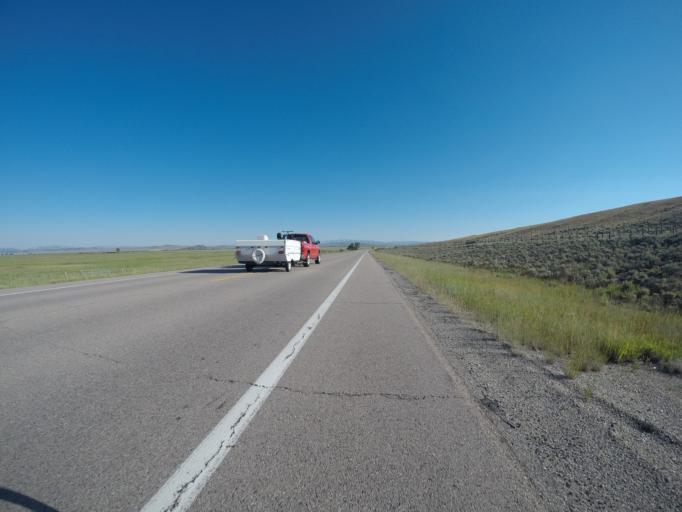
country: US
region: Wyoming
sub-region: Sublette County
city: Pinedale
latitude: 42.9482
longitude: -110.0851
